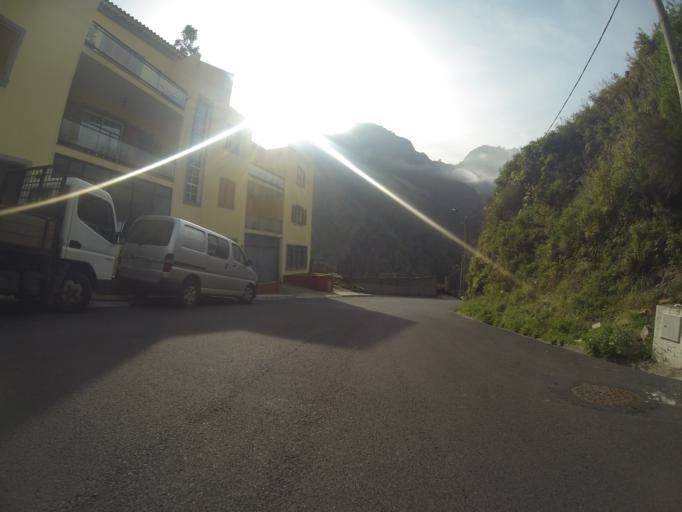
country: PT
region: Madeira
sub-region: Camara de Lobos
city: Curral das Freiras
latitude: 32.7274
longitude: -16.9658
